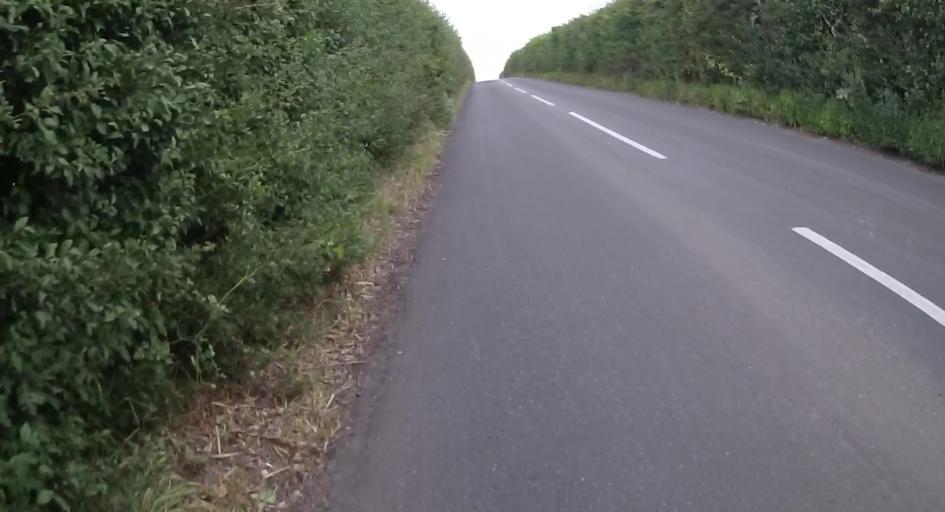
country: GB
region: England
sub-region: Hampshire
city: Kings Worthy
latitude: 51.1419
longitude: -1.3070
